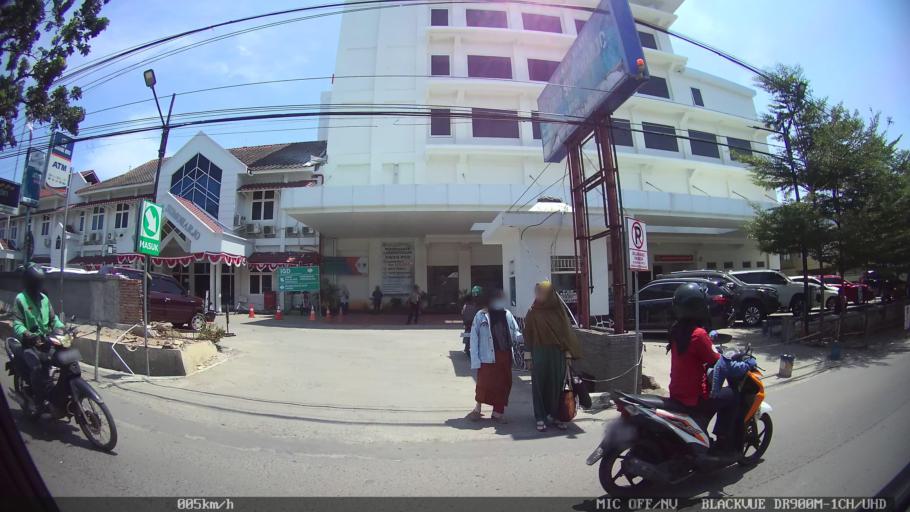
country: ID
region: Lampung
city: Kedaton
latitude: -5.3910
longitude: 105.2767
